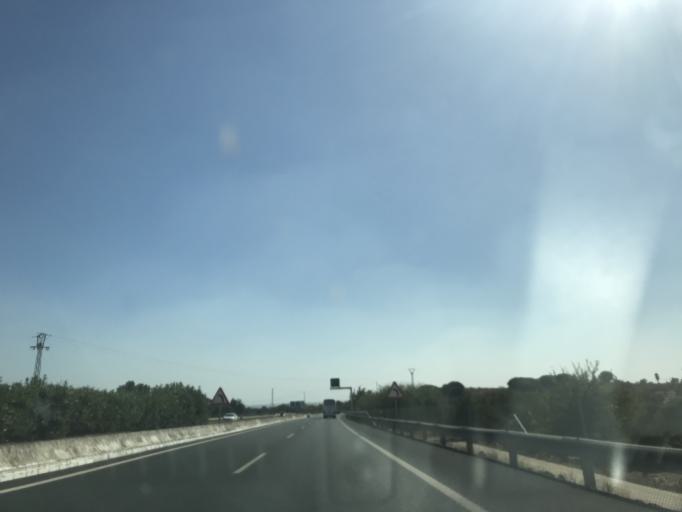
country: ES
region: Andalusia
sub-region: Provincia de Sevilla
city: Alcala de Guadaira
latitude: 37.3347
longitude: -5.8210
